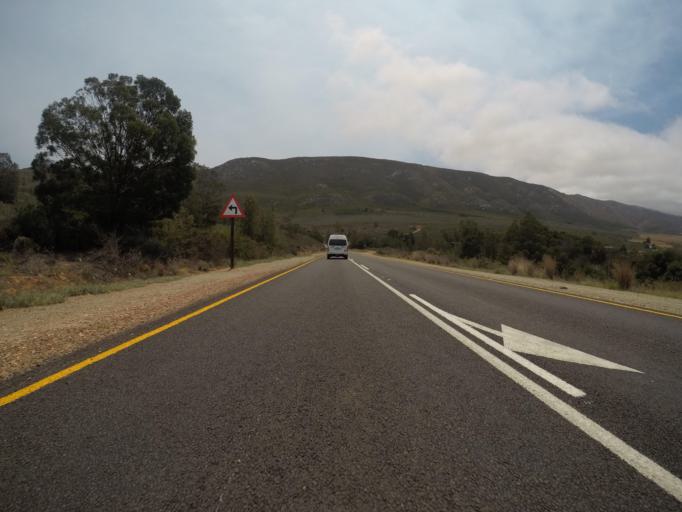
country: ZA
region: Western Cape
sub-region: Eden District Municipality
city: Knysna
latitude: -33.7647
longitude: 22.9624
